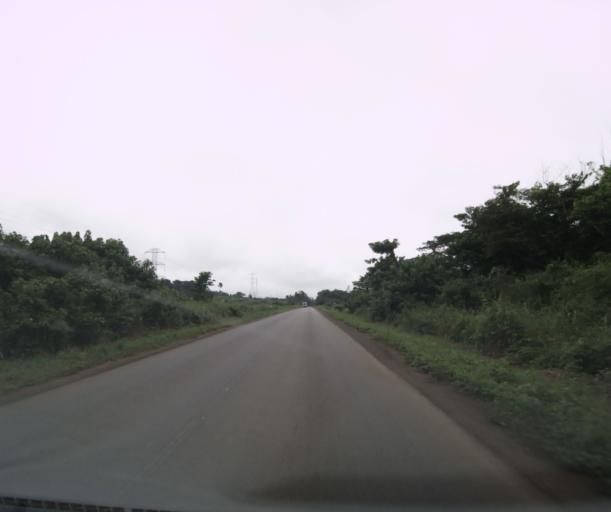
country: CM
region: Littoral
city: Edea
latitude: 3.6794
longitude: 10.1089
